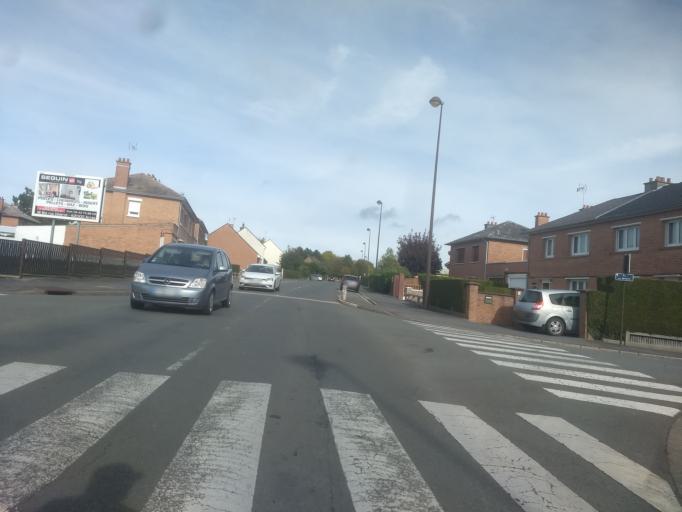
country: FR
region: Nord-Pas-de-Calais
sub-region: Departement du Pas-de-Calais
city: Dainville
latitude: 50.2903
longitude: 2.7420
